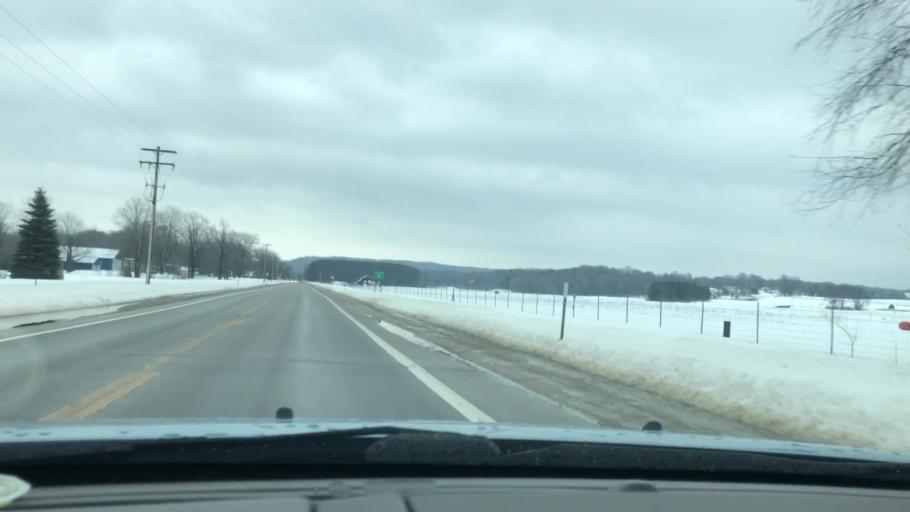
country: US
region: Michigan
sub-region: Charlevoix County
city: East Jordan
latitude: 45.1325
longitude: -85.1096
